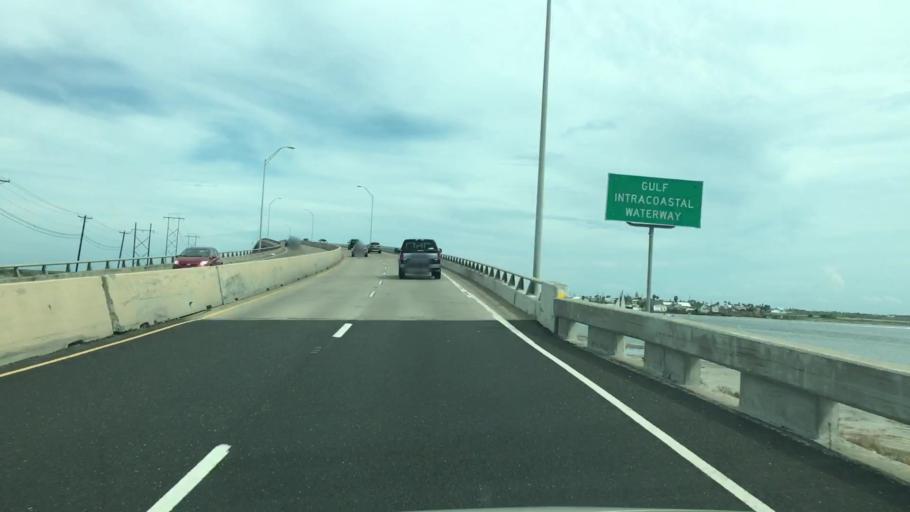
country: US
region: Texas
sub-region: Nueces County
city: Corpus Christi
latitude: 27.6370
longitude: -97.2444
